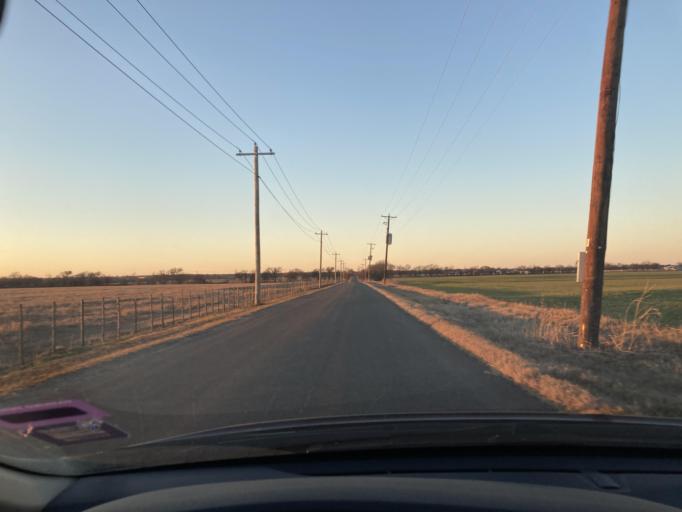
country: US
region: Texas
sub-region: Ellis County
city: Nash
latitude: 32.2816
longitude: -96.9039
